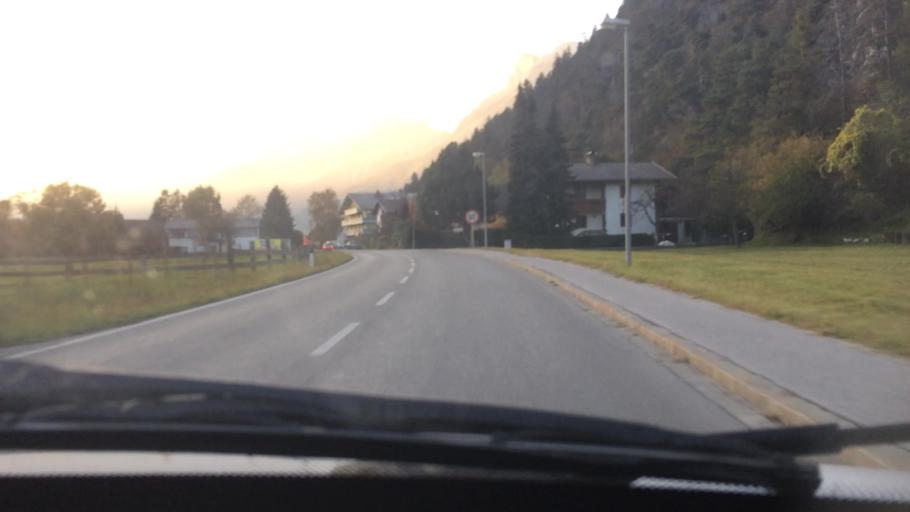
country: AT
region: Tyrol
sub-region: Politischer Bezirk Innsbruck Land
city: Hatting
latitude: 47.2924
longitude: 11.1591
